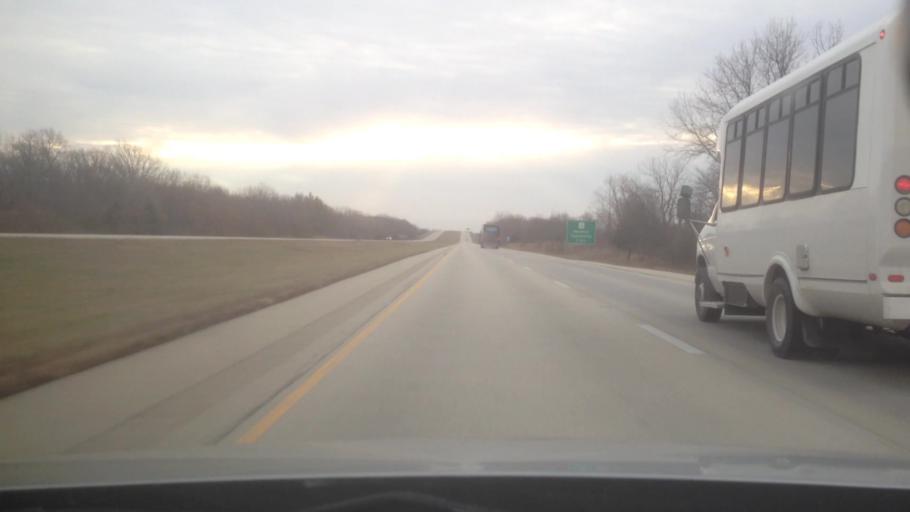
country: US
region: Illinois
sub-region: Macon County
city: Harristown
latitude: 39.8100
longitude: -89.0241
